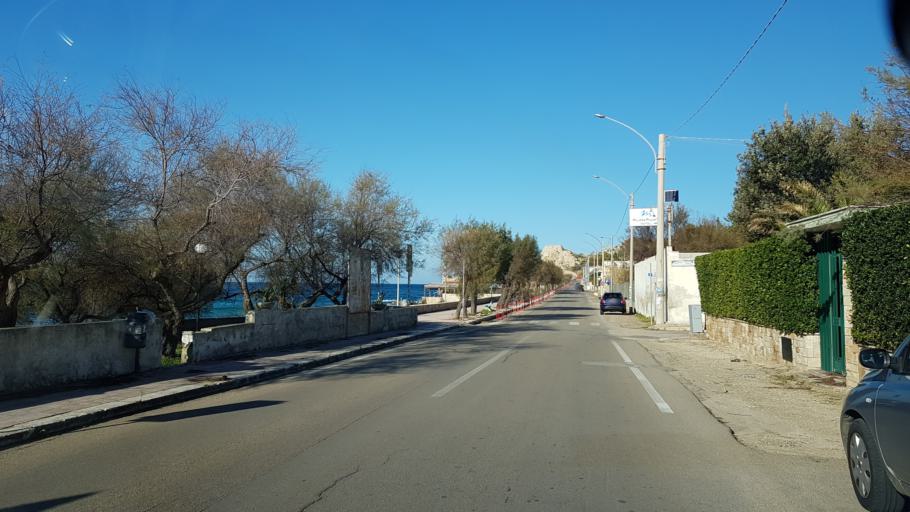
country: IT
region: Apulia
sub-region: Provincia di Lecce
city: Nardo
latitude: 40.1104
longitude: 18.0095
